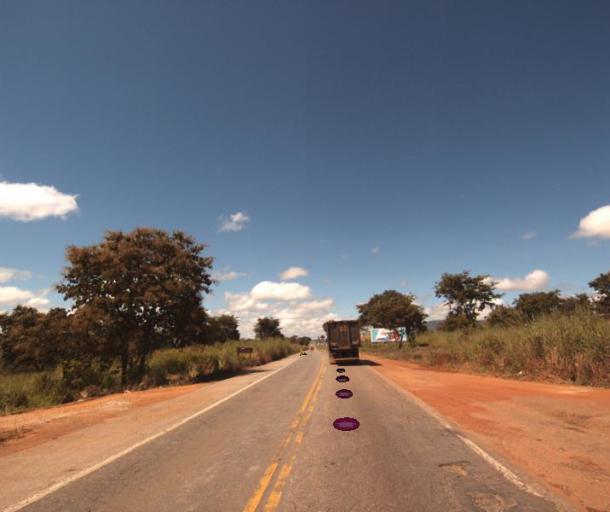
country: BR
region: Goias
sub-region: Jaragua
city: Jaragua
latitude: -15.7239
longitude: -49.3280
